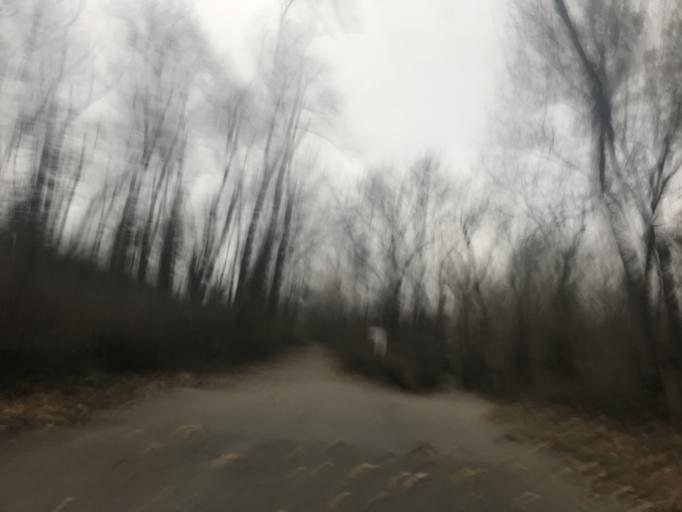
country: US
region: Indiana
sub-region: Clark County
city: Jeffersonville
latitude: 38.2649
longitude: -85.7206
